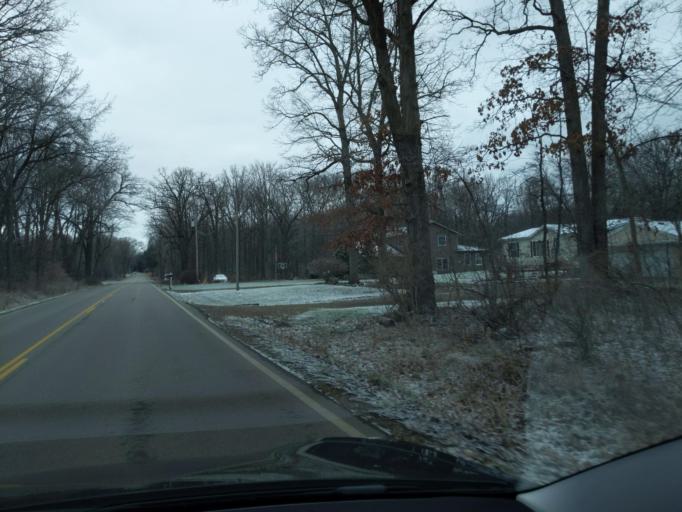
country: US
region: Michigan
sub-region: Jackson County
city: Spring Arbor
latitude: 42.2284
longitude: -84.5169
